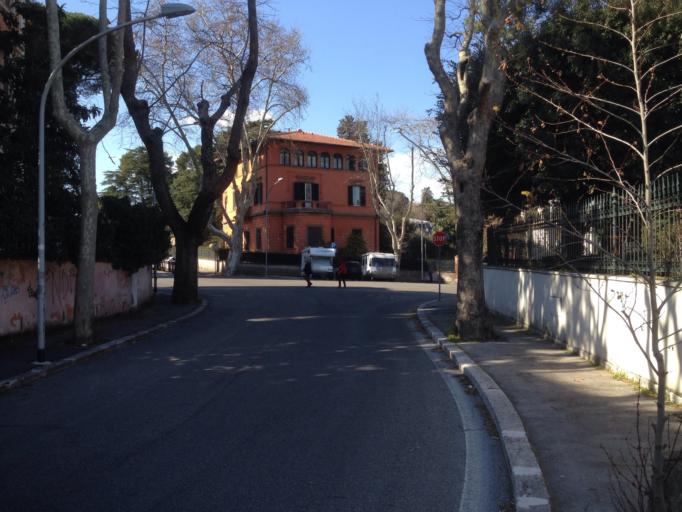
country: VA
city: Vatican City
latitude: 41.8877
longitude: 12.4641
